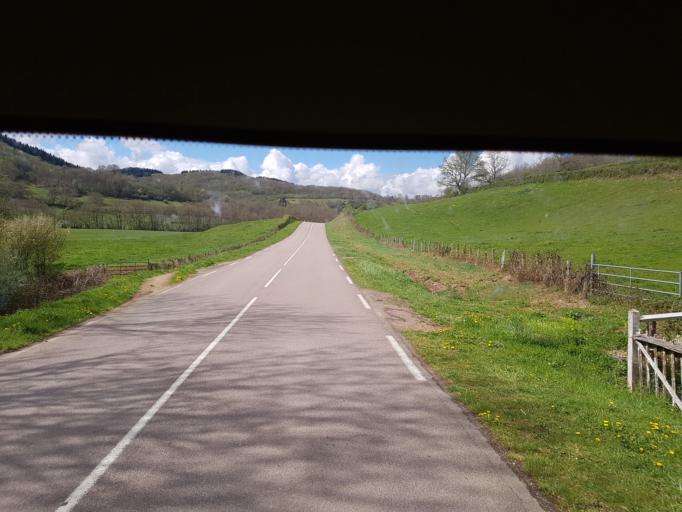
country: FR
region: Bourgogne
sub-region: Departement de Saone-et-Loire
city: Autun
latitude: 47.0958
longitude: 4.2342
